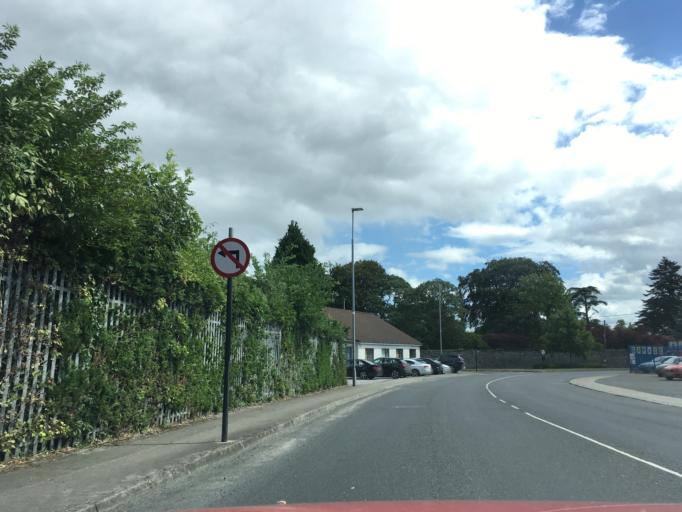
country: IE
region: Munster
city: Cahir
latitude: 52.3744
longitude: -7.9319
